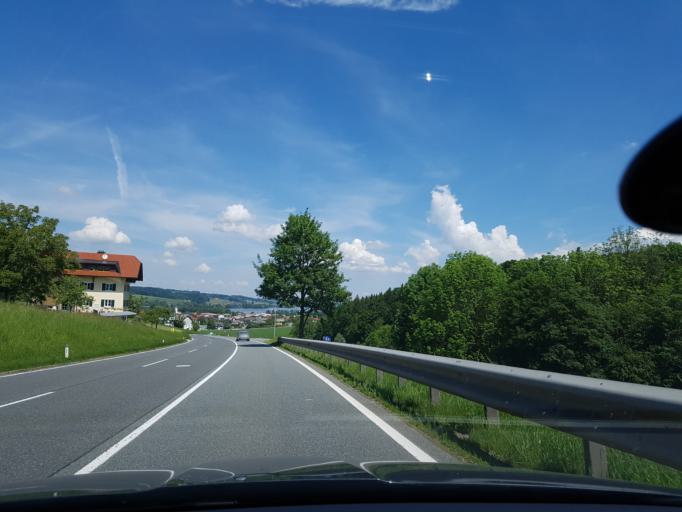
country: AT
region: Salzburg
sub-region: Politischer Bezirk Salzburg-Umgebung
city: Obertrum am See
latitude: 47.9252
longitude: 13.0833
